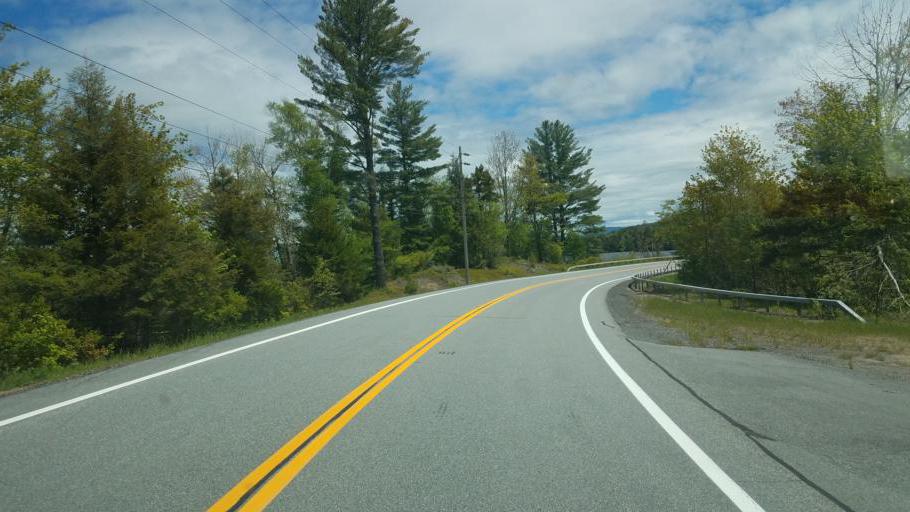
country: US
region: New York
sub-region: Hamilton County
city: Lake Pleasant
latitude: 43.8071
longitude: -74.6125
